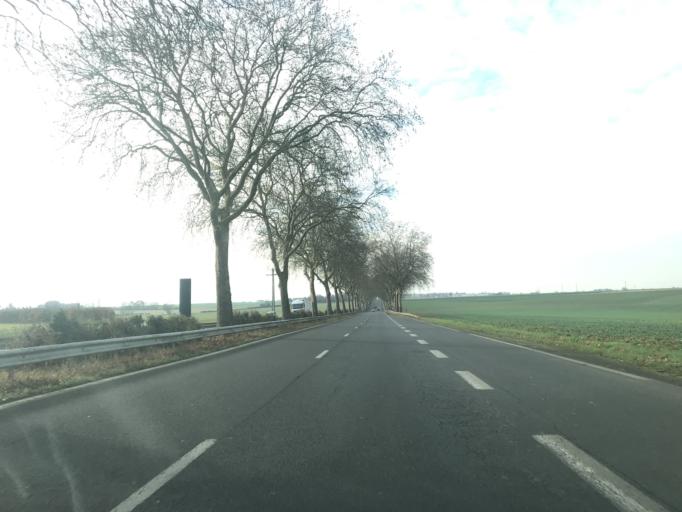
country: FR
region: Poitou-Charentes
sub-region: Departement des Deux-Sevres
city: Chauray
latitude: 46.3496
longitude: -0.3452
